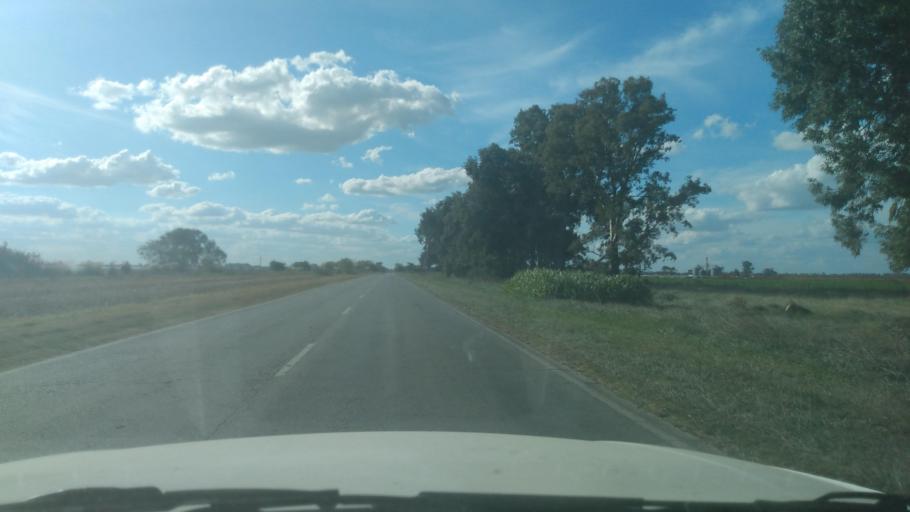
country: AR
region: Buenos Aires
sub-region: Partido de Navarro
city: Navarro
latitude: -34.9784
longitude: -59.3165
